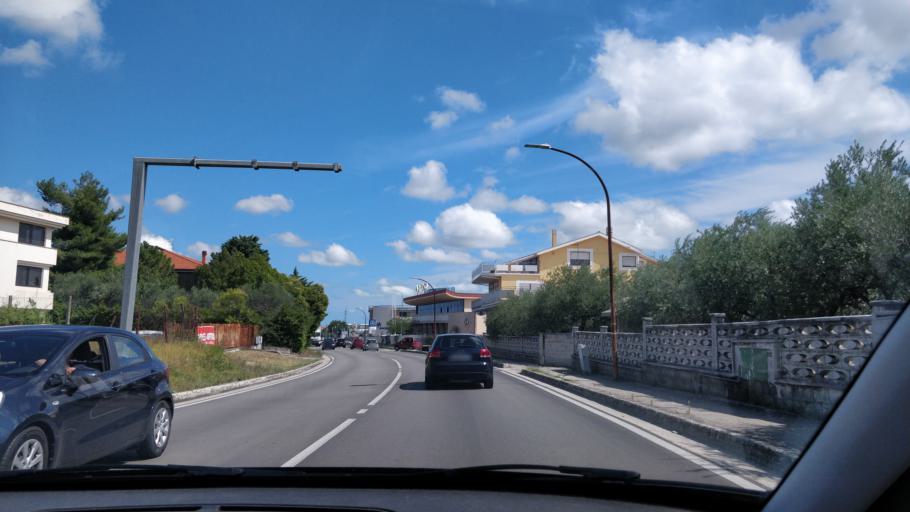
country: IT
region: Abruzzo
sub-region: Provincia di Chieti
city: Lanciano
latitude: 42.2370
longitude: 14.4090
